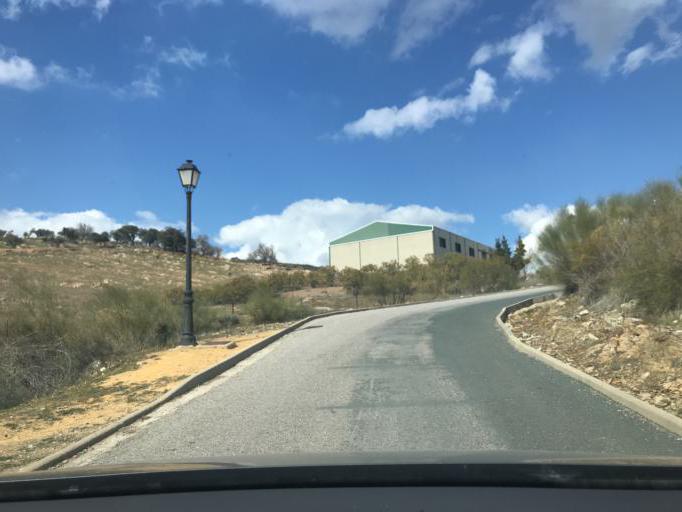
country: ES
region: Andalusia
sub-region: Provincia de Sevilla
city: Guadalcanal
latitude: 38.1003
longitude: -5.8190
